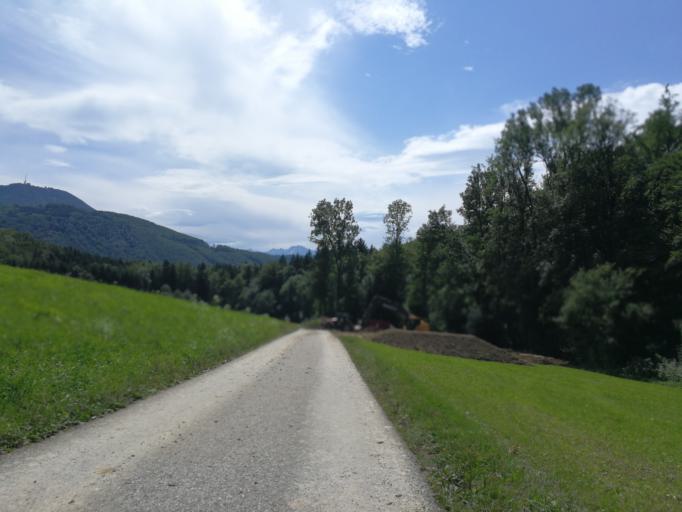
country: AT
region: Salzburg
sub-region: Politischer Bezirk Salzburg-Umgebung
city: Hallwang
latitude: 47.8488
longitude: 13.0845
